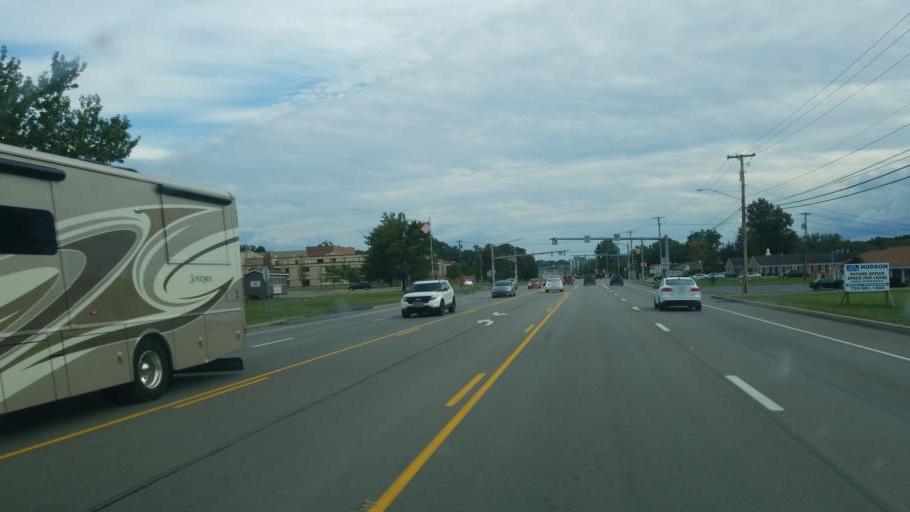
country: US
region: Pennsylvania
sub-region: Mercer County
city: Hermitage
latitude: 41.2444
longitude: -80.4499
